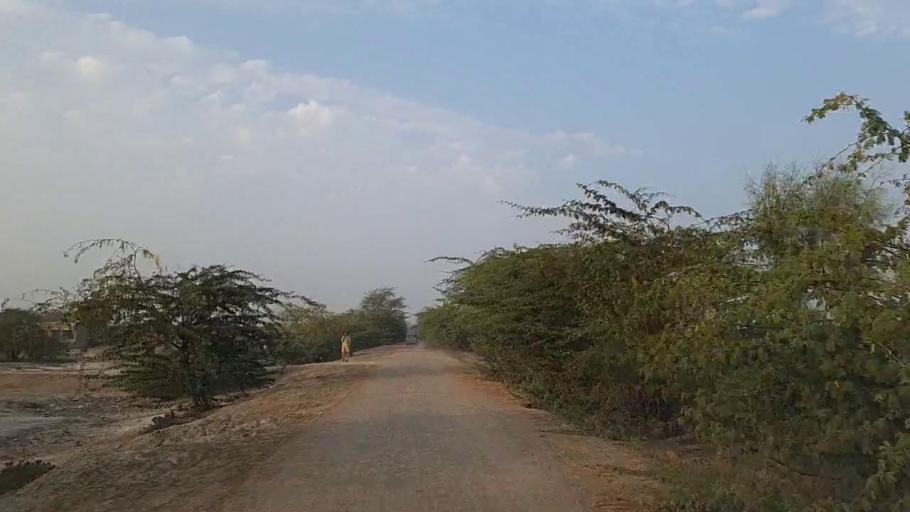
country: PK
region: Sindh
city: Jam Sahib
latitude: 26.3162
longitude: 68.6090
